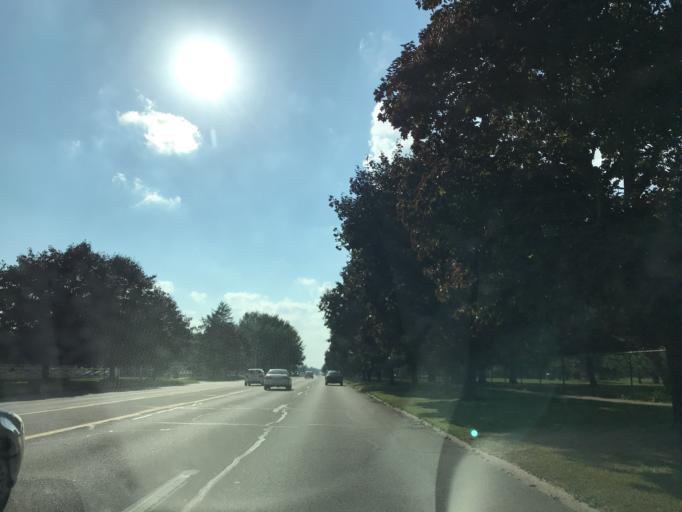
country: US
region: Michigan
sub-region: Wayne County
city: Livonia
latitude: 42.3970
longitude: -83.3916
